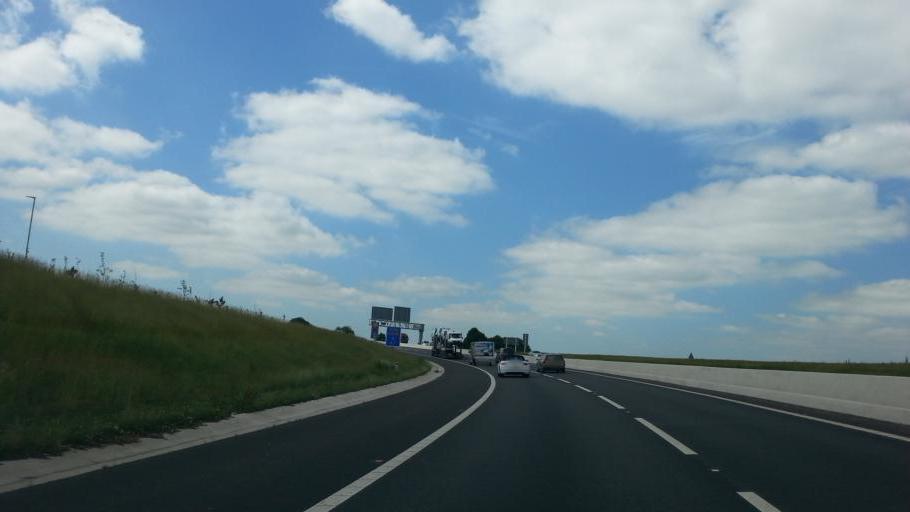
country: GB
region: England
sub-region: Trafford
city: Bowdon
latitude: 53.3676
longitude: -2.3864
